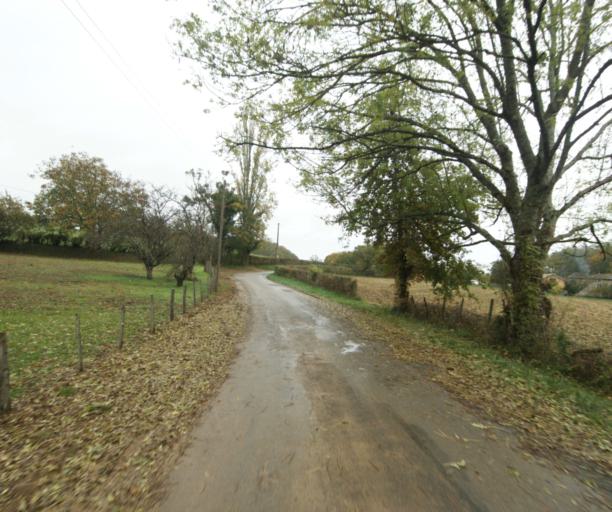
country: FR
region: Bourgogne
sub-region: Departement de Saone-et-Loire
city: Saint-Martin-Belle-Roche
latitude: 46.4760
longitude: 4.8462
